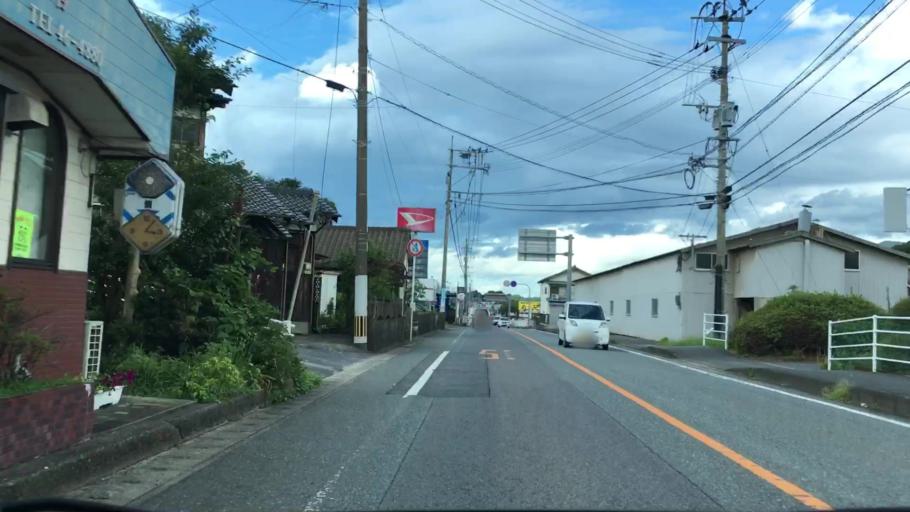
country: JP
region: Saga Prefecture
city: Imaricho-ko
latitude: 33.1975
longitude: 129.8505
